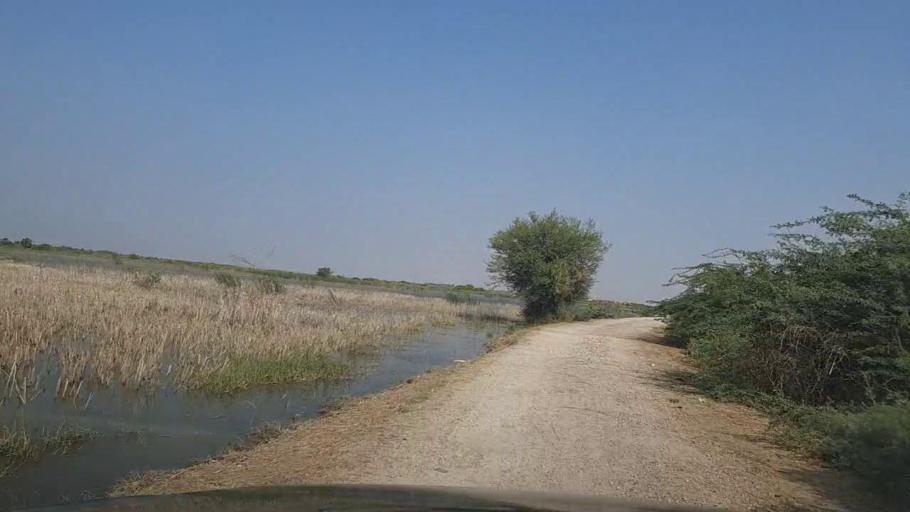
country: PK
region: Sindh
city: Thatta
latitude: 24.6378
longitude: 67.8135
